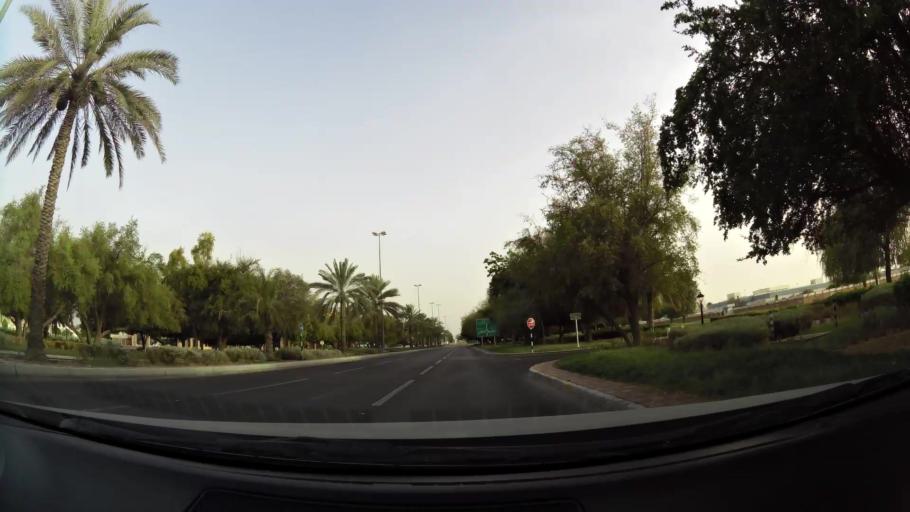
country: OM
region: Al Buraimi
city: Al Buraymi
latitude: 24.2438
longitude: 55.7391
